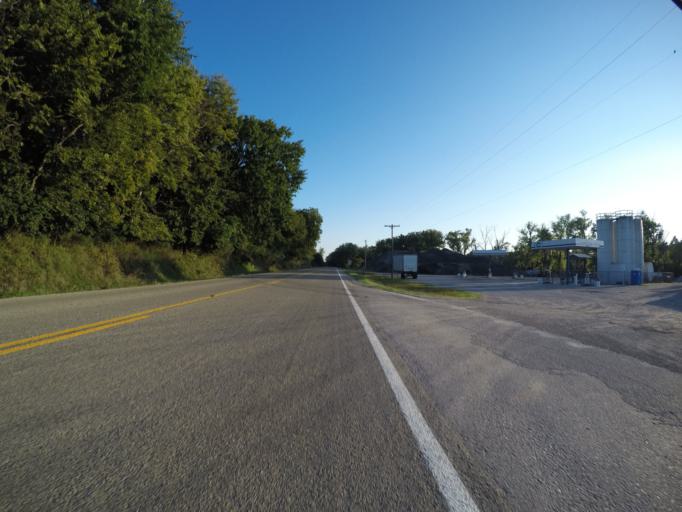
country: US
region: Kansas
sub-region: Riley County
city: Manhattan
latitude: 39.1670
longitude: -96.5539
